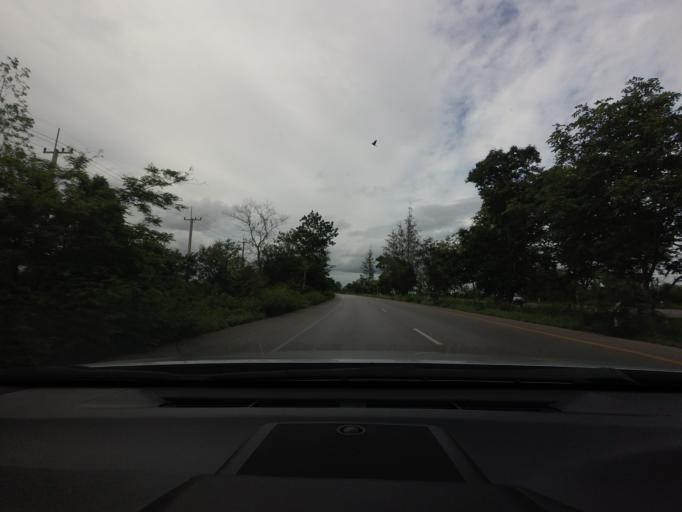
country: TH
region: Phetchaburi
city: Cha-am
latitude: 12.7268
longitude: 99.9256
